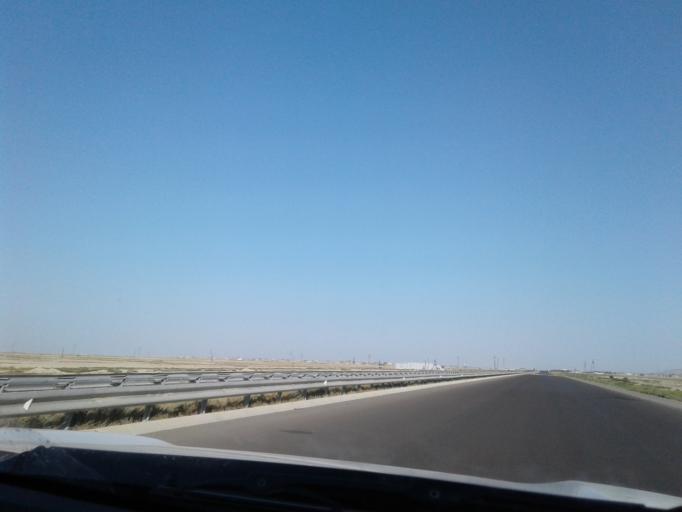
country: TM
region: Balkan
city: Serdar
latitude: 39.0141
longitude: 56.2268
